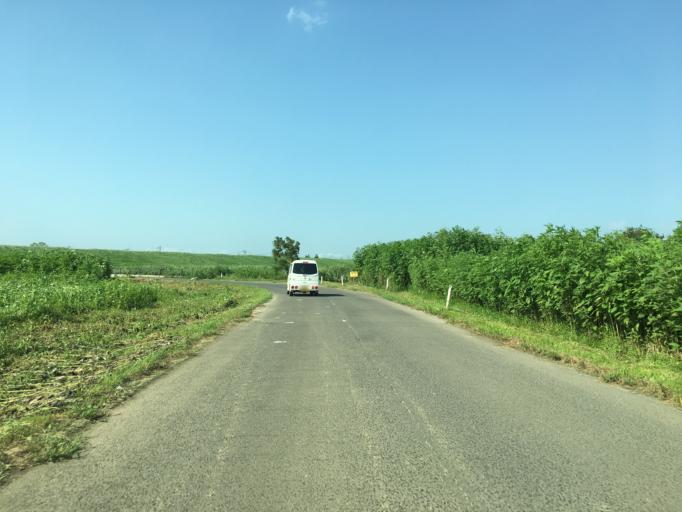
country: JP
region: Miyagi
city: Kakuda
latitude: 37.9667
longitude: 140.7887
